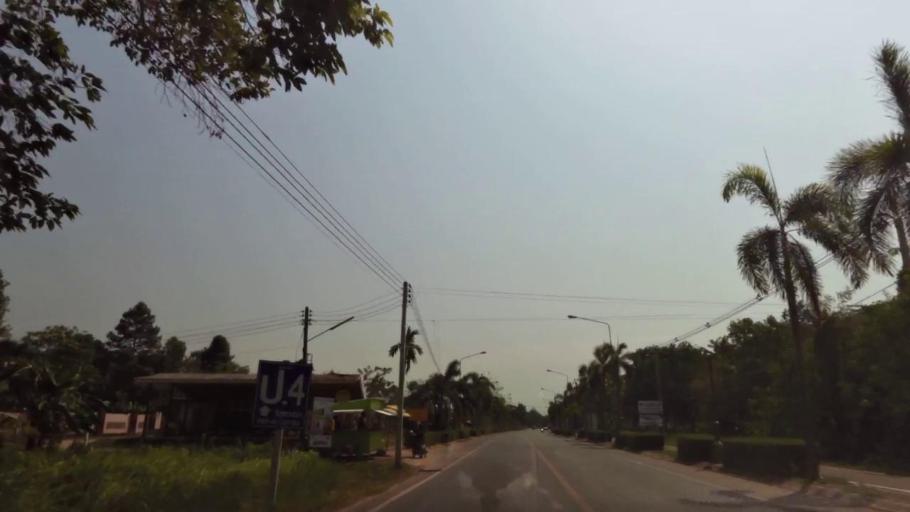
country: TH
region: Chanthaburi
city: Tha Mai
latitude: 12.5486
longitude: 101.9269
